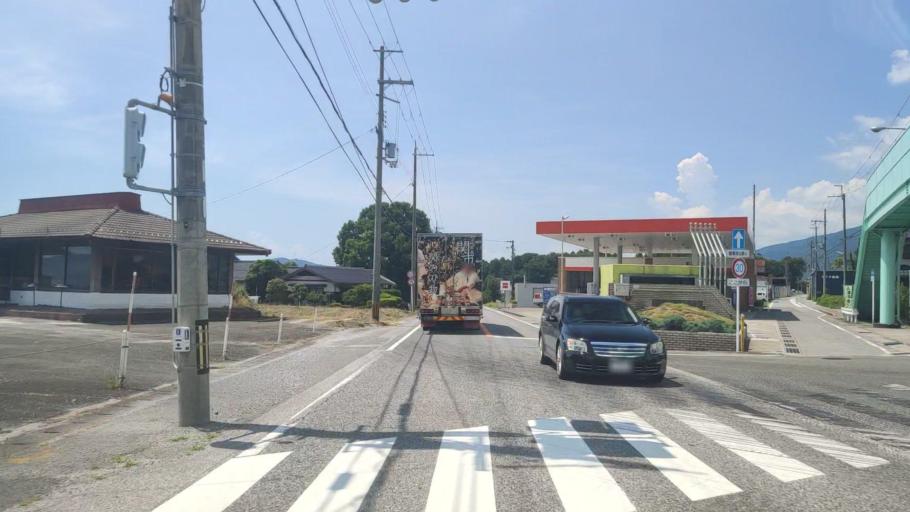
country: JP
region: Shiga Prefecture
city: Nagahama
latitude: 35.3774
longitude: 136.3801
